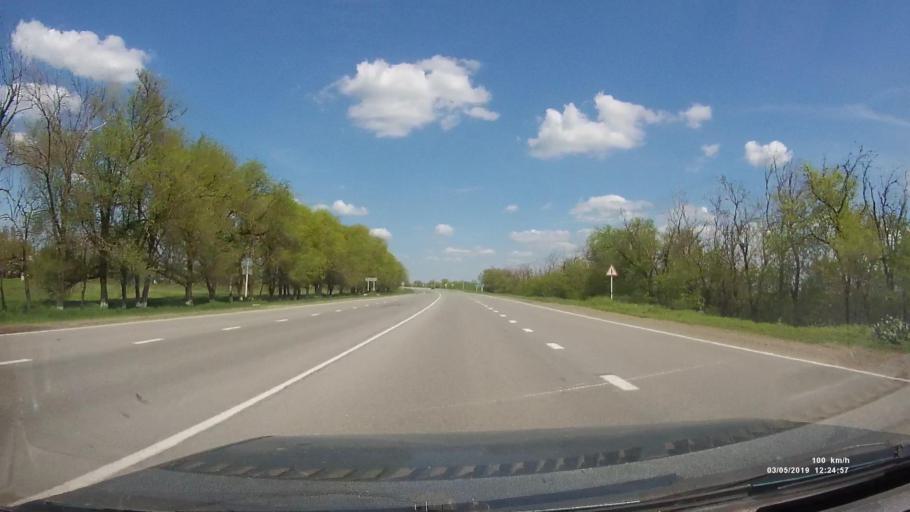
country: RU
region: Rostov
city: Semikarakorsk
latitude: 47.4259
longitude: 40.7069
